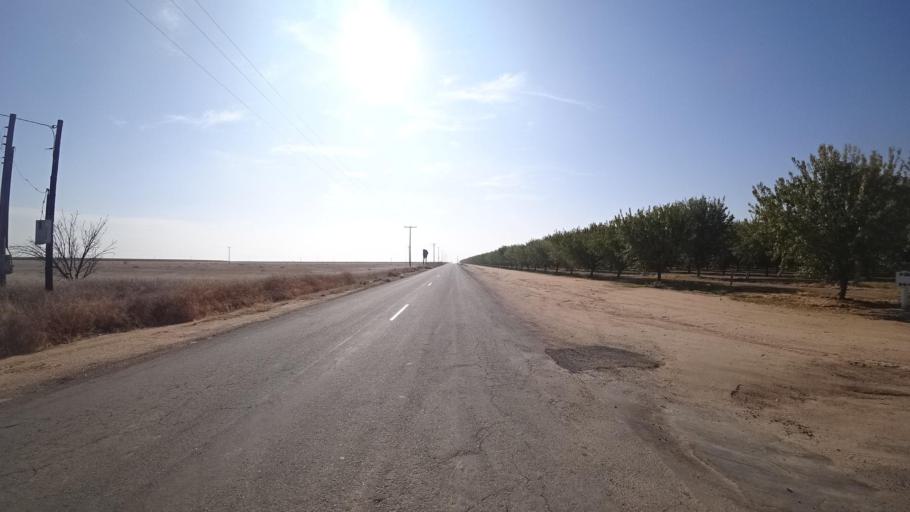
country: US
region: California
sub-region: Kern County
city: McFarland
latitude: 35.6656
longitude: -119.1692
